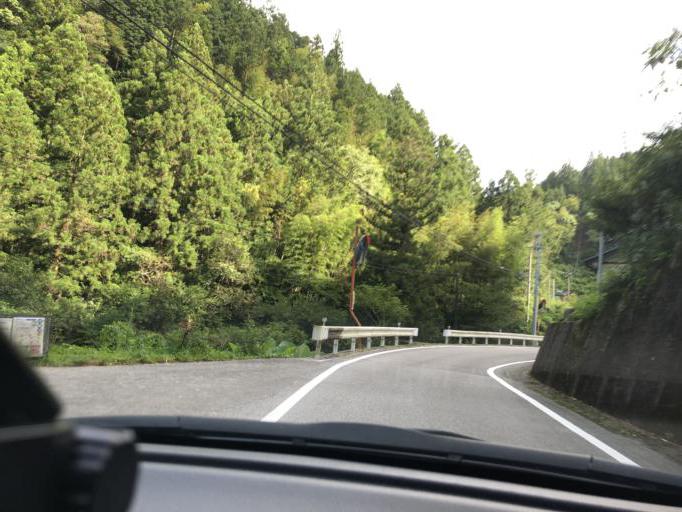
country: JP
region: Kochi
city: Kochi-shi
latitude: 33.6173
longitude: 133.4970
